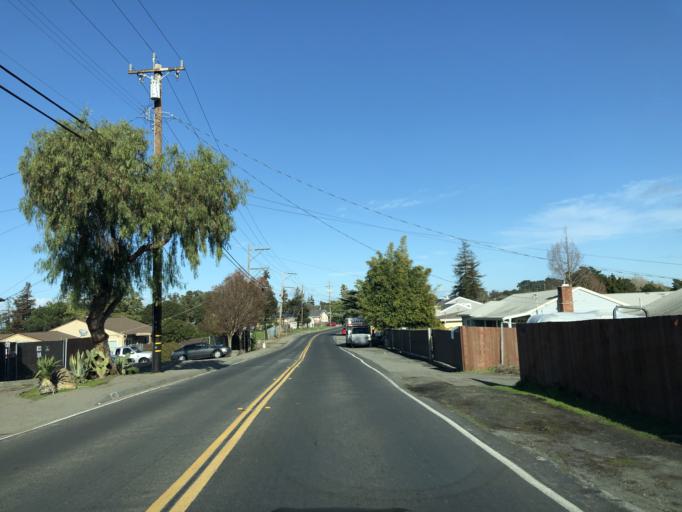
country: US
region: California
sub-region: Contra Costa County
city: El Sobrante
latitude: 37.9777
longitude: -122.3060
